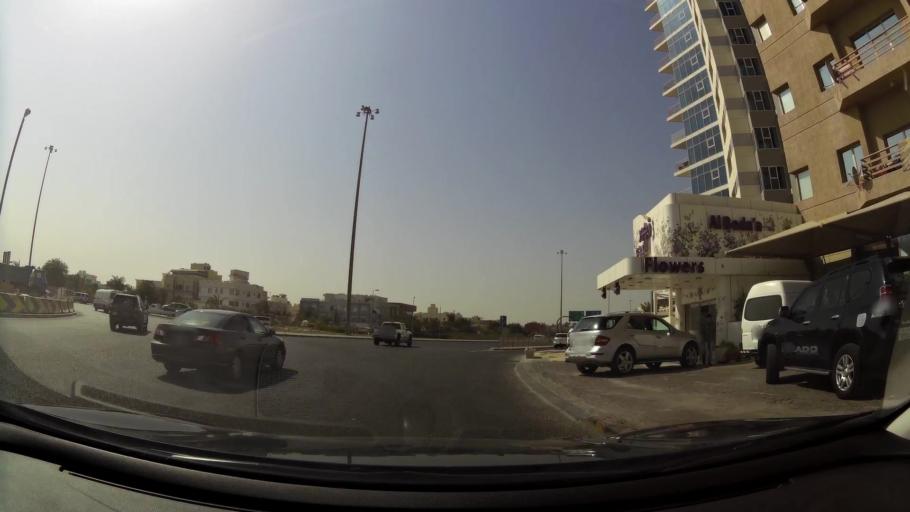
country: KW
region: Muhafazat Hawalli
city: As Salimiyah
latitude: 29.3238
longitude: 48.0882
